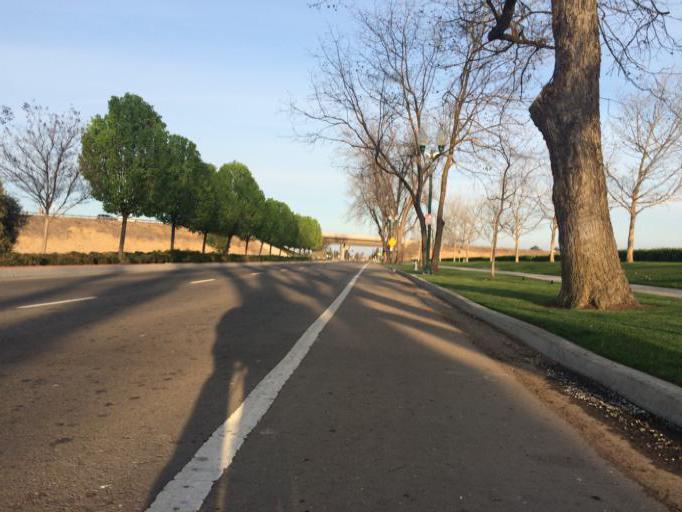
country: US
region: California
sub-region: Fresno County
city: Sunnyside
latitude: 36.7503
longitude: -119.6778
